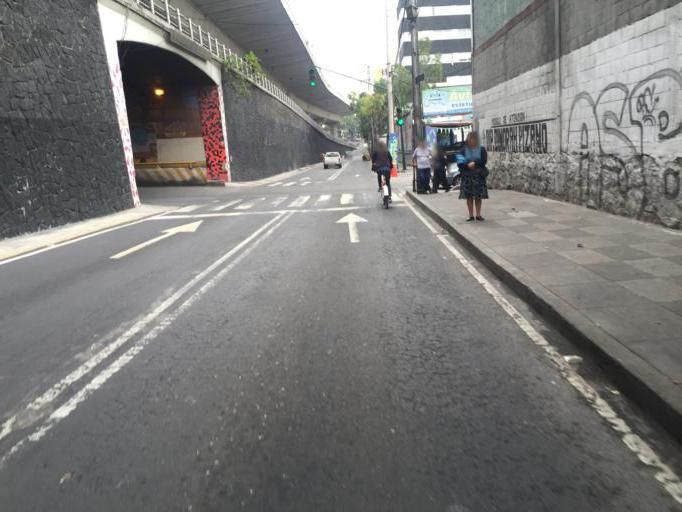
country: MX
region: Mexico City
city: Colonia del Valle
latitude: 19.3909
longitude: -99.1889
